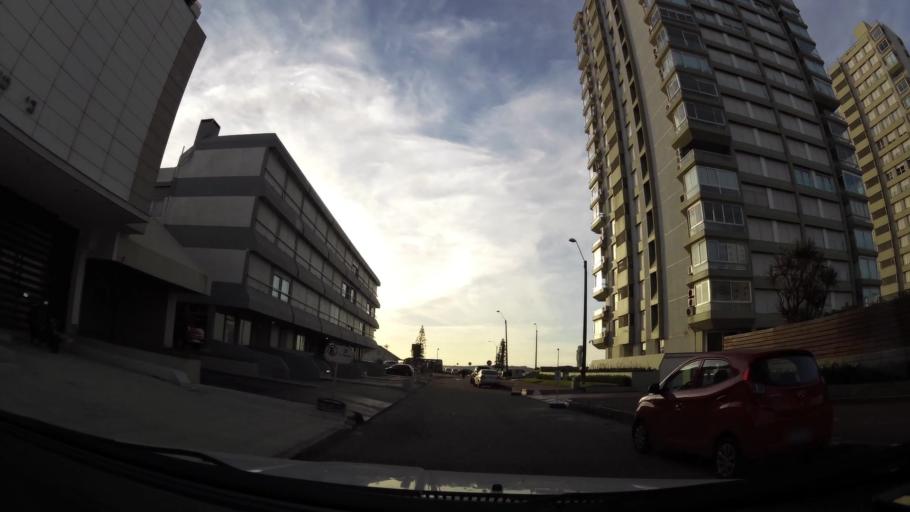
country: UY
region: Maldonado
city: Punta del Este
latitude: -34.9568
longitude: -54.9396
